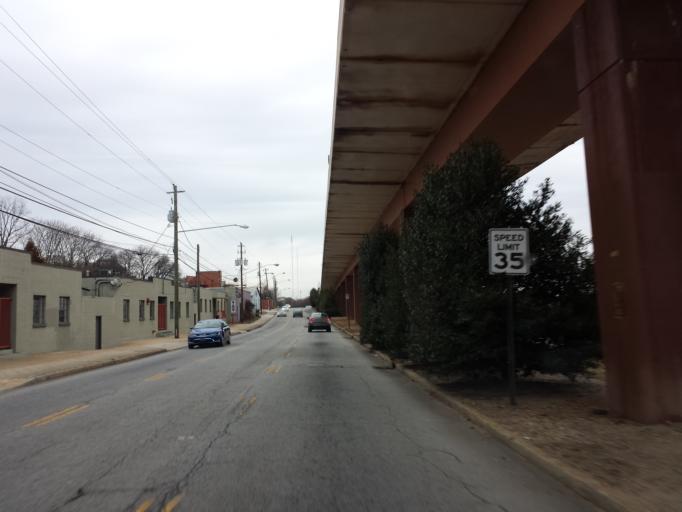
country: US
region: Georgia
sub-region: Fulton County
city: Atlanta
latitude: 33.7540
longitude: -84.3610
